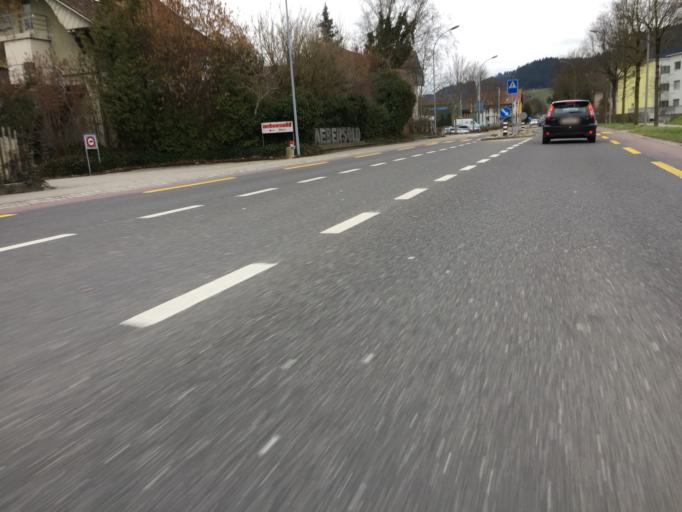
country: CH
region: Bern
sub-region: Emmental District
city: Oberburg
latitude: 47.0476
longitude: 7.6223
